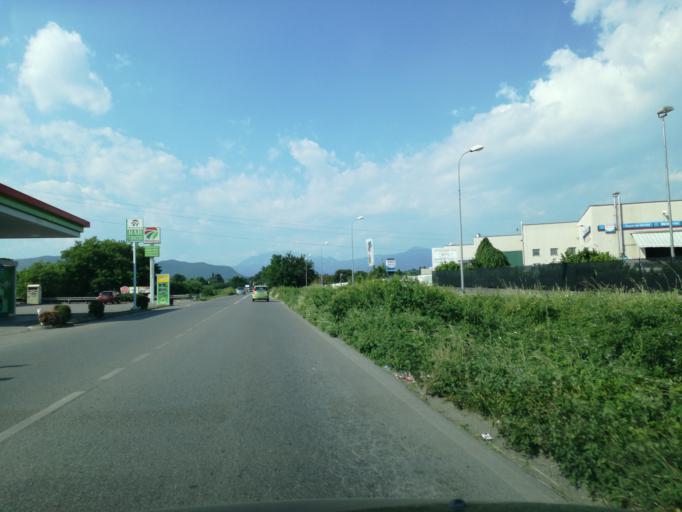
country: IT
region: Lombardy
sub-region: Provincia di Lecco
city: Cernusco Lombardone
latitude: 45.6847
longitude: 9.3989
